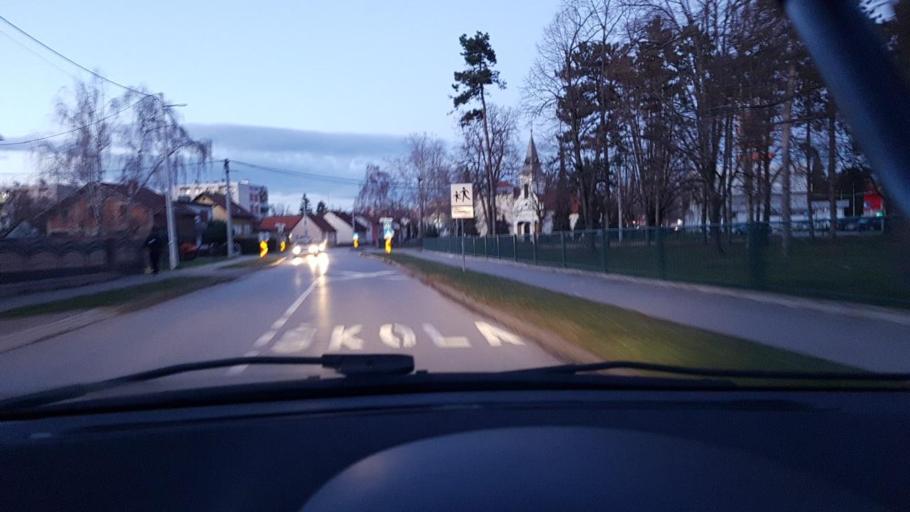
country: HR
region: Zagrebacka
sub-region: Grad Velika Gorica
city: Velika Gorica
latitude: 45.7122
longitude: 16.0724
